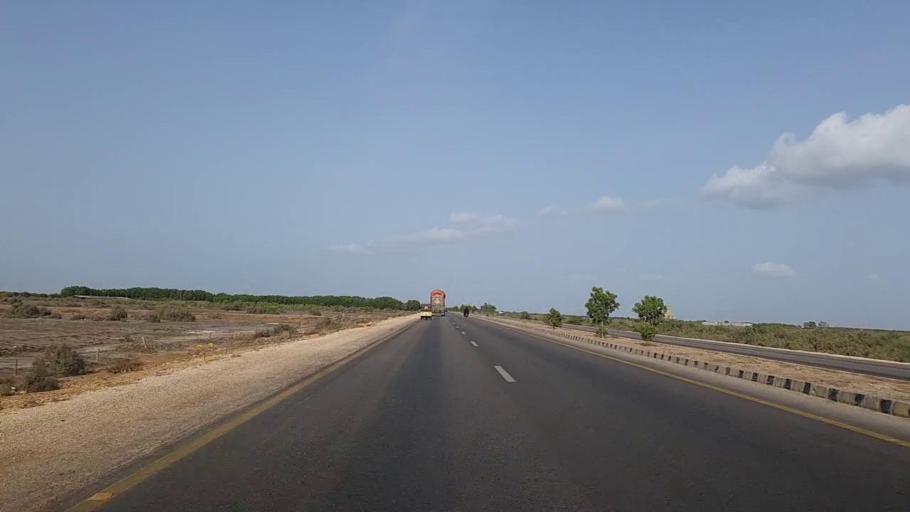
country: PK
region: Sindh
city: Gharo
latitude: 24.7374
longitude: 67.7193
